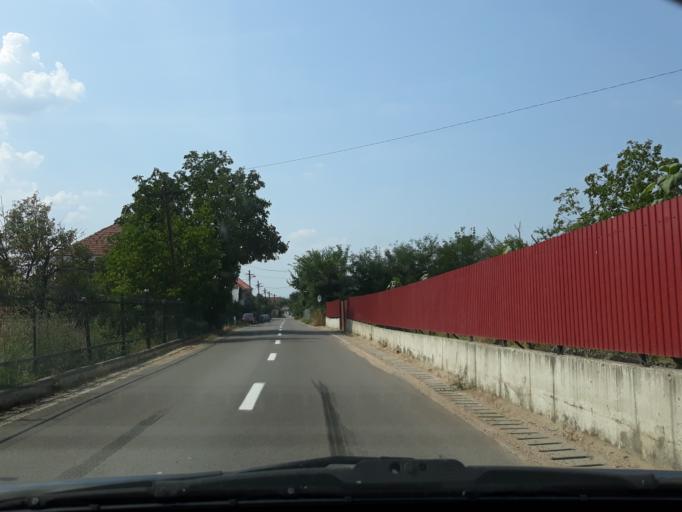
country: RO
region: Bihor
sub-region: Comuna Pietroasa
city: Pietroasa
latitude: 46.5901
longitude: 22.5620
